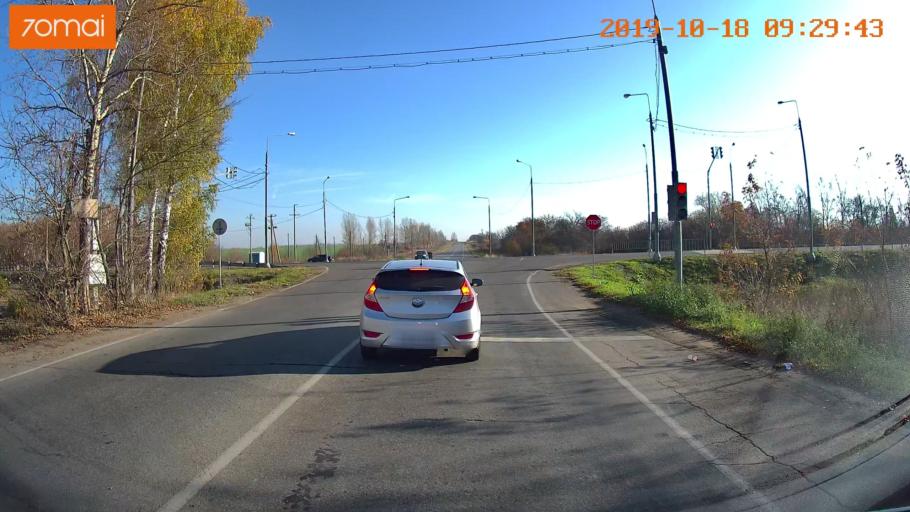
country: RU
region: Tula
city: Yefremov
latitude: 53.1387
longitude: 38.1592
